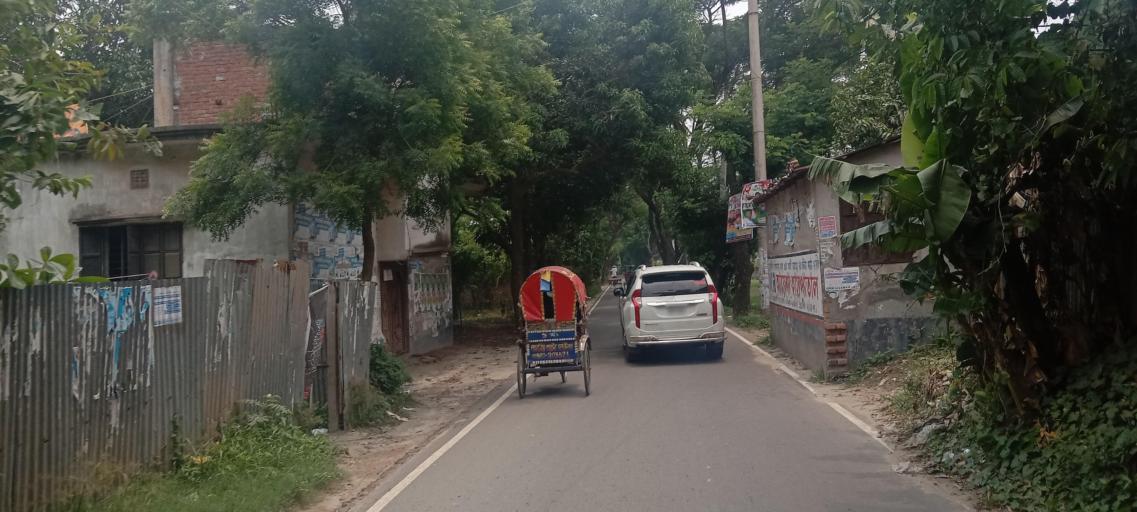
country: BD
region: Dhaka
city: Azimpur
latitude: 23.7162
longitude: 90.3447
